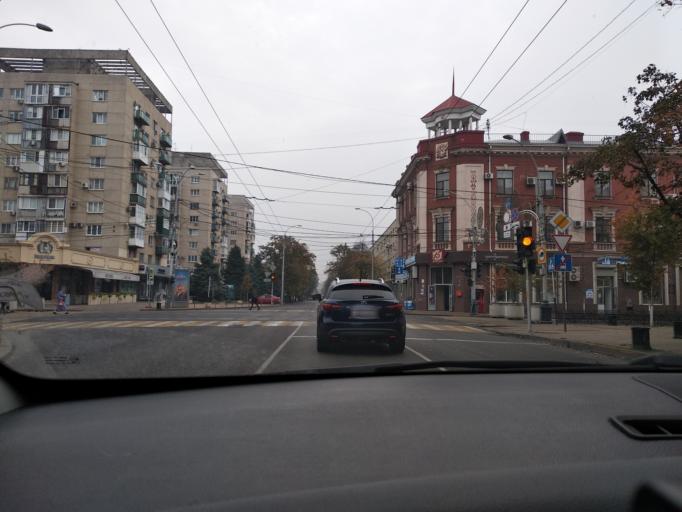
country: RU
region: Krasnodarskiy
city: Krasnodar
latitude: 45.0209
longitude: 38.9688
